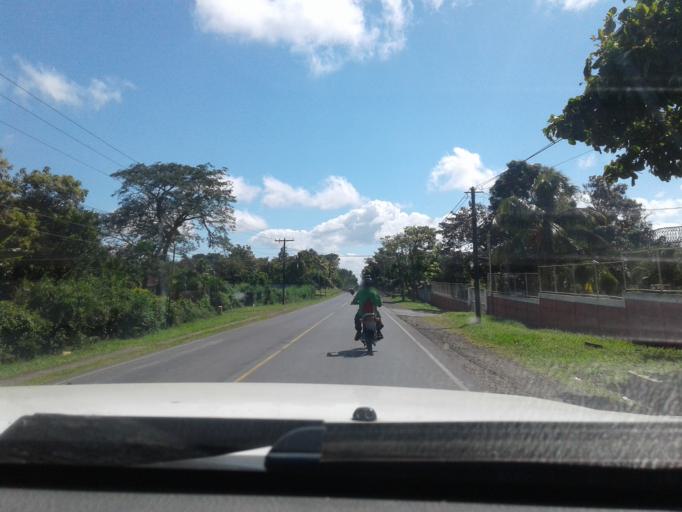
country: NI
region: Carazo
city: Jinotepe
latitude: 11.8269
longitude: -86.1706
